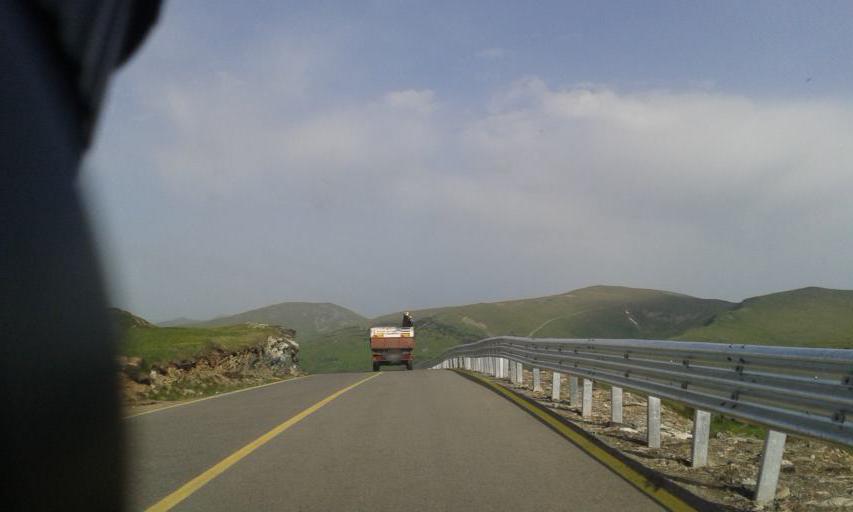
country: RO
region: Gorj
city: Novaci-Straini
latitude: 45.3591
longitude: 23.6637
